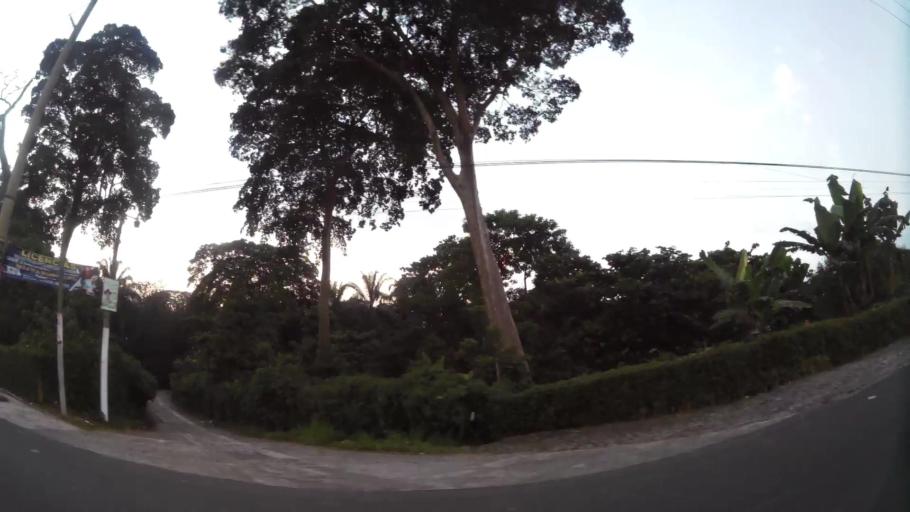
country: GT
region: Retalhuleu
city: San Martin Zapotitlan
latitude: 14.6071
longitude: -91.6079
